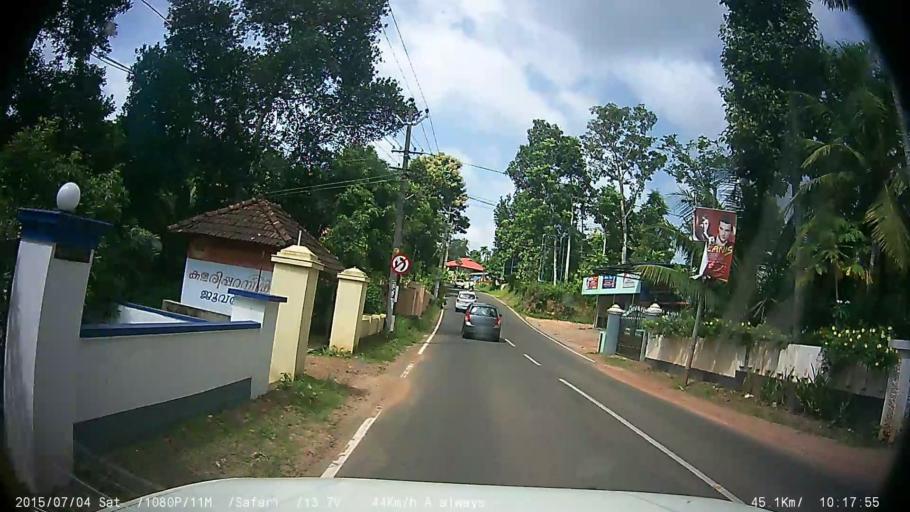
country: IN
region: Kerala
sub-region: Kottayam
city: Changanacheri
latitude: 9.4585
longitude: 76.5768
